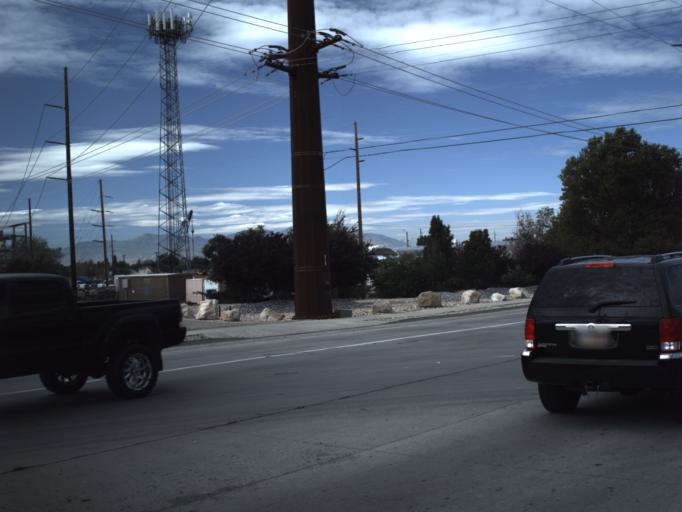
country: US
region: Utah
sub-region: Davis County
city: West Bountiful
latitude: 40.8843
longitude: -111.9018
